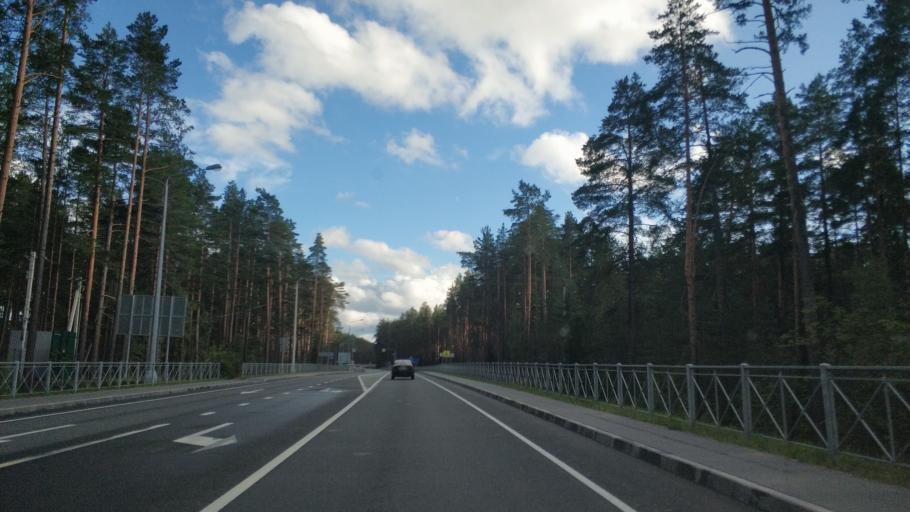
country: RU
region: Leningrad
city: Priozersk
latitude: 60.9965
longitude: 30.1821
